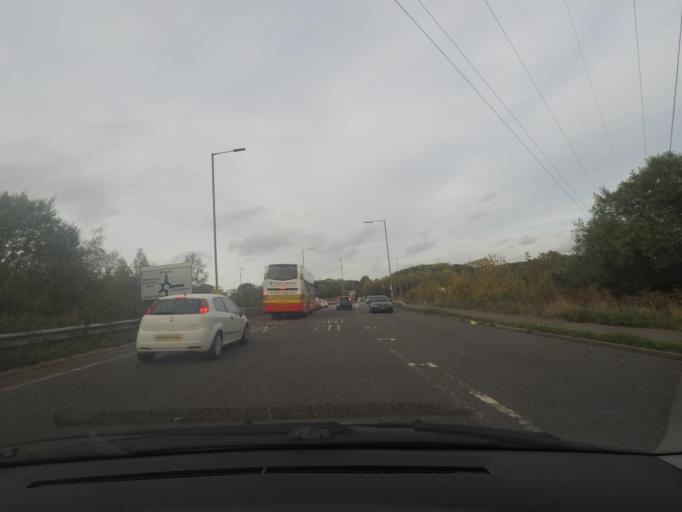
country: GB
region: England
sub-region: Sheffield
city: Chapletown
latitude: 53.4859
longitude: -1.4944
